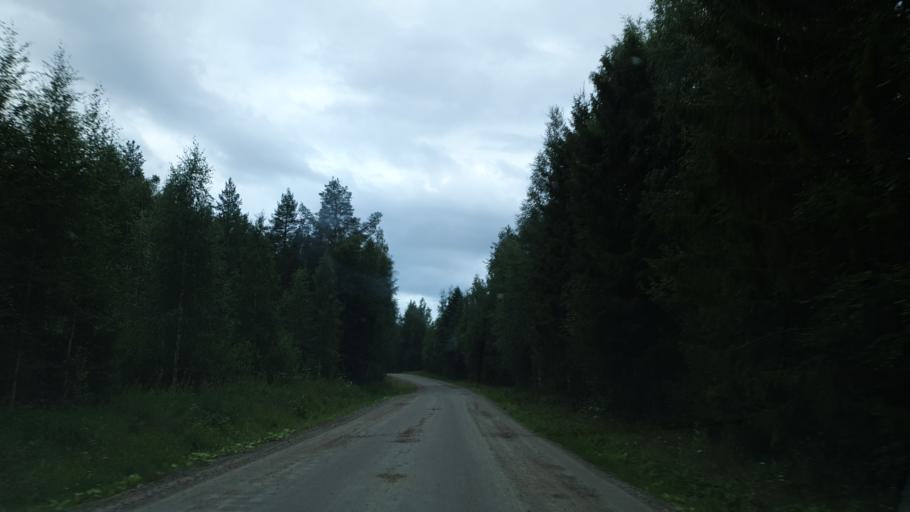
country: FI
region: Kainuu
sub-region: Kehys-Kainuu
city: Kuhmo
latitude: 64.1983
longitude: 29.3666
